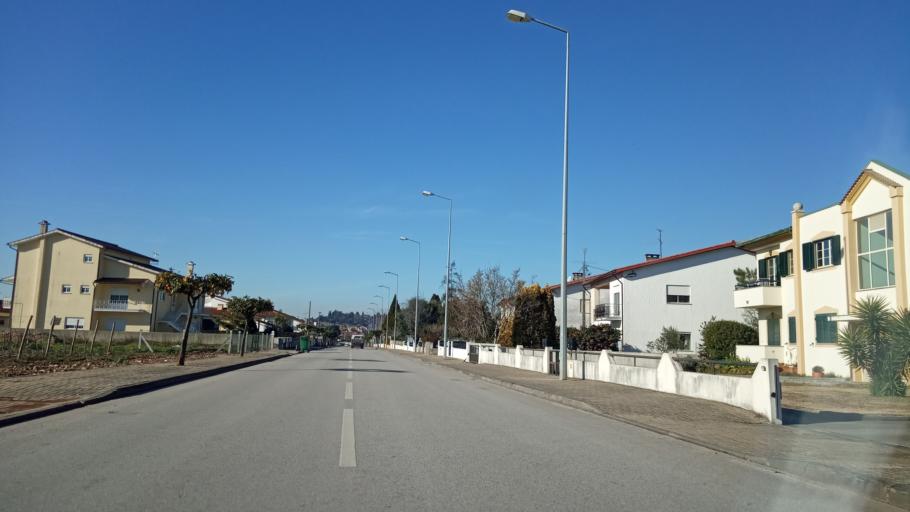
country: PT
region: Aveiro
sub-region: Anadia
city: Anadia
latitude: 40.4337
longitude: -8.4273
